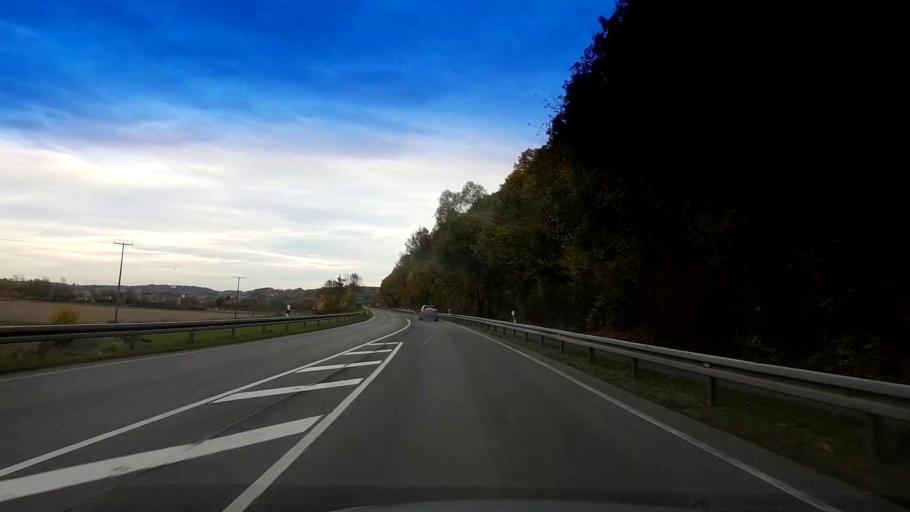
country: DE
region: Bavaria
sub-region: Regierungsbezirk Unterfranken
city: Stettfeld
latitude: 49.9432
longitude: 10.7274
